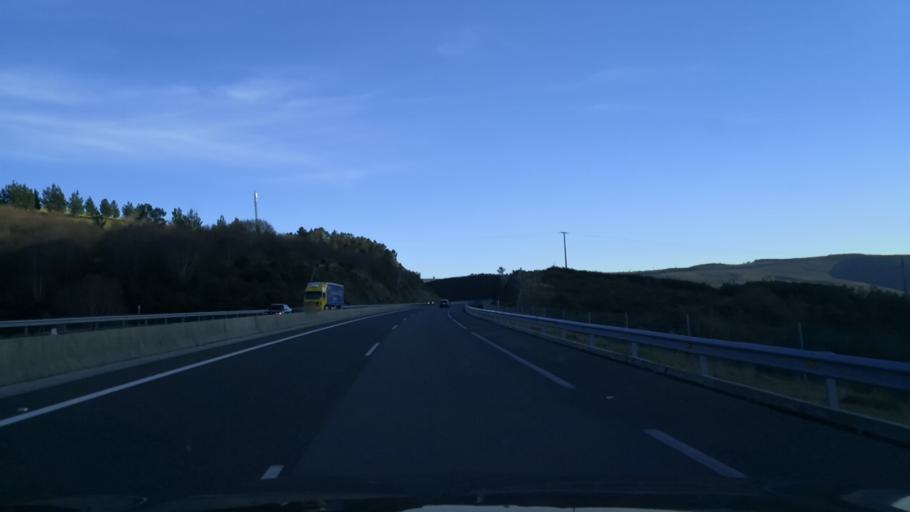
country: ES
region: Galicia
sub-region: Provincia de Pontevedra
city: Dozon
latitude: 42.5953
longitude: -8.0863
